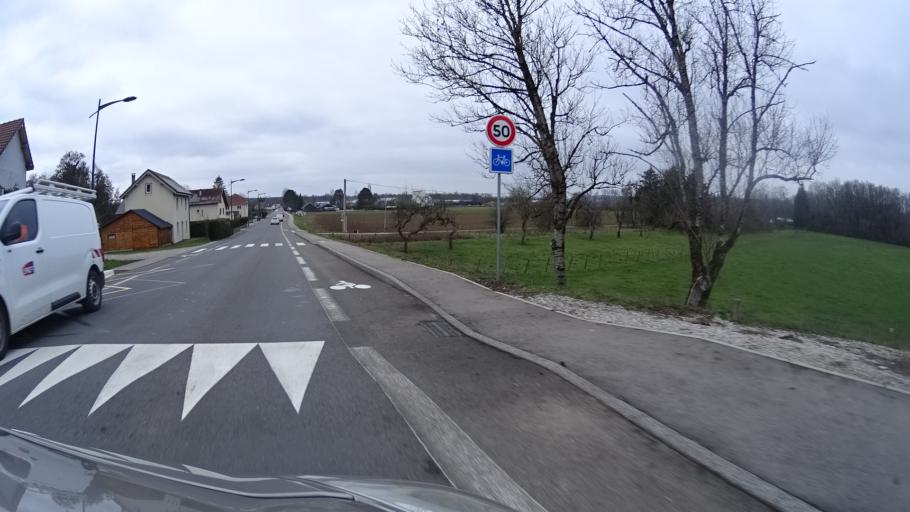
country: FR
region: Franche-Comte
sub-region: Departement du Doubs
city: Saone
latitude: 47.2142
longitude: 6.1080
